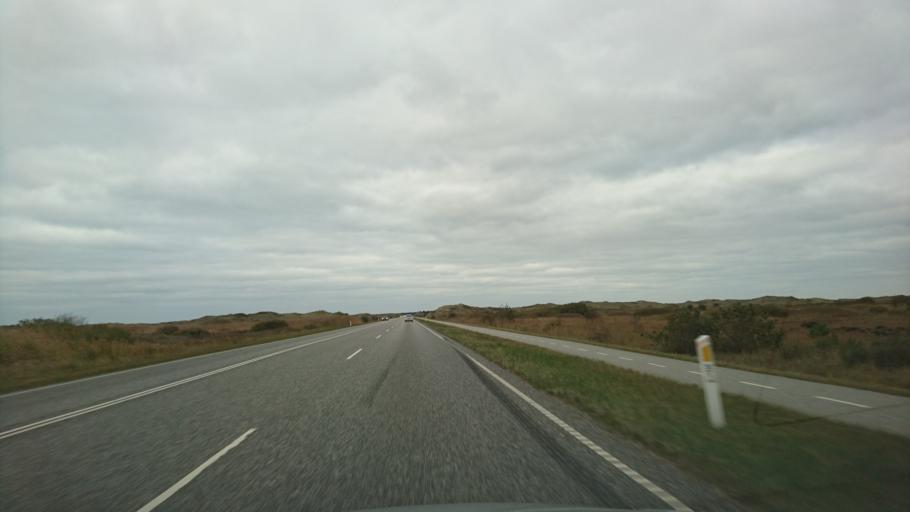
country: DK
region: North Denmark
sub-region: Frederikshavn Kommune
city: Skagen
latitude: 57.6802
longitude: 10.4622
